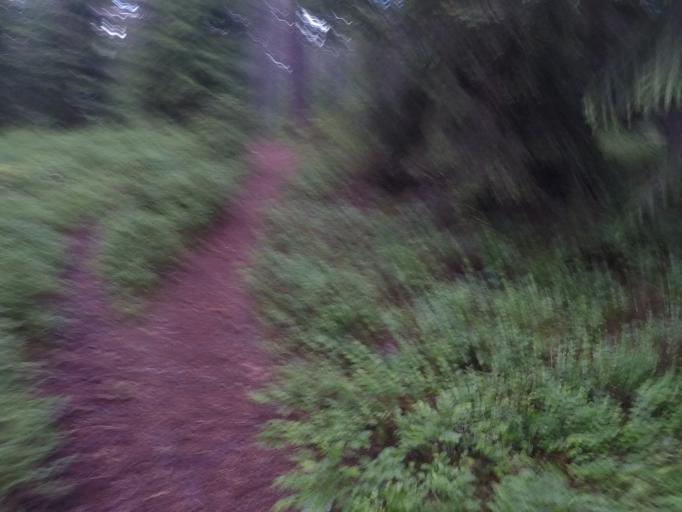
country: SE
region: Soedermanland
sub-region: Eskilstuna Kommun
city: Hallbybrunn
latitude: 59.3967
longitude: 16.4051
